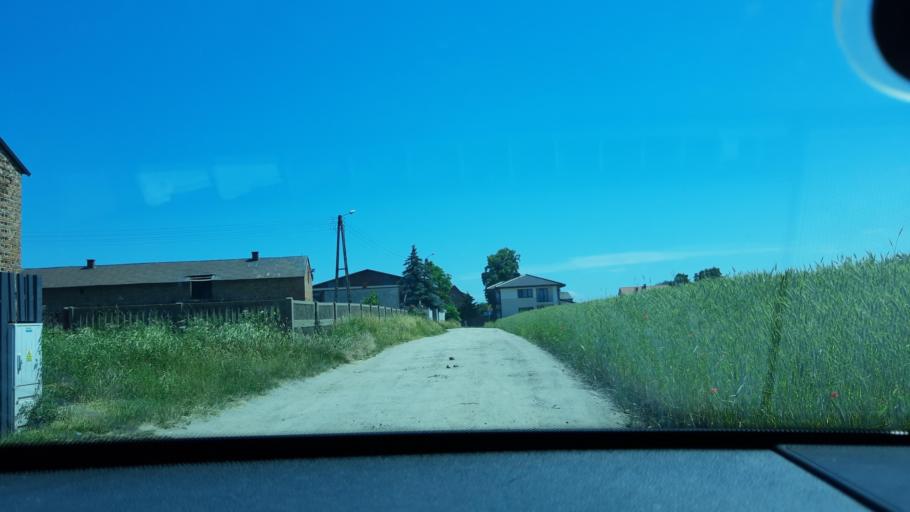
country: PL
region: Lodz Voivodeship
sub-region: Powiat sieradzki
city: Sieradz
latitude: 51.5709
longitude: 18.7437
